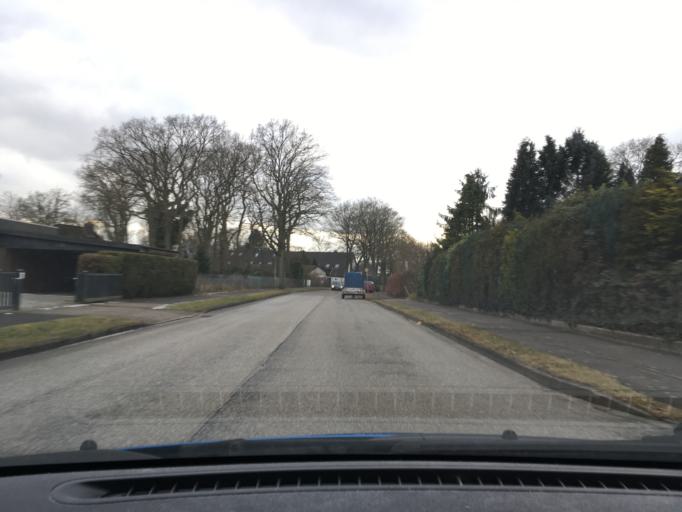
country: DE
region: Schleswig-Holstein
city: Wedel
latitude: 53.5911
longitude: 9.7273
